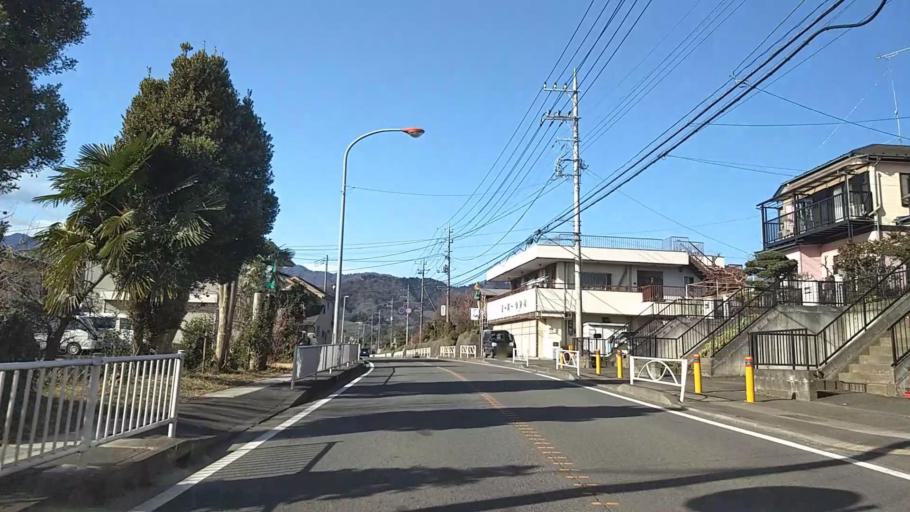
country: JP
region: Kanagawa
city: Atsugi
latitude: 35.4709
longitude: 139.3220
